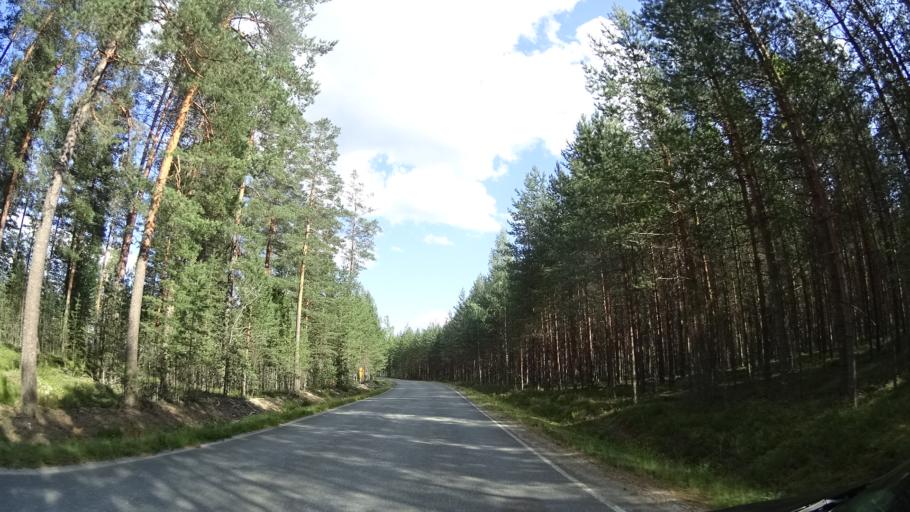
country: FI
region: Uusimaa
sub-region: Helsinki
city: Kaerkoelae
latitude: 60.7405
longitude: 24.0891
